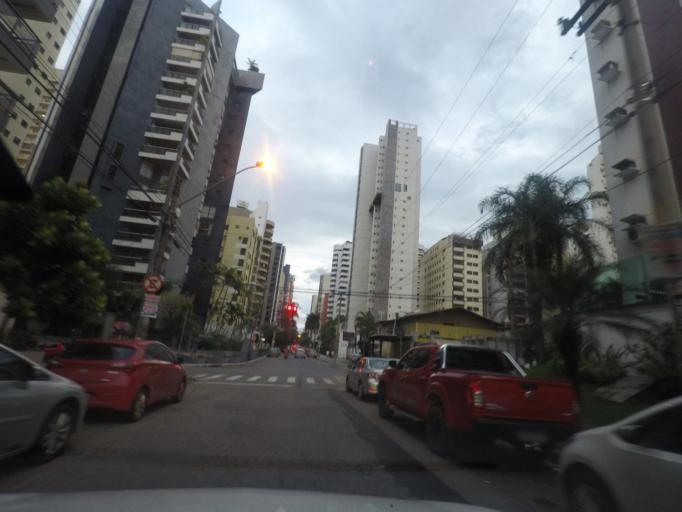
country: BR
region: Goias
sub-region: Goiania
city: Goiania
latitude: -16.7125
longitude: -49.2706
